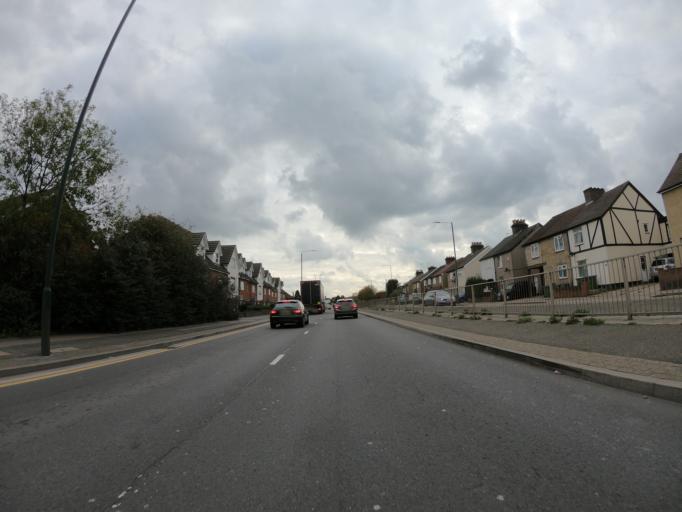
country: GB
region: England
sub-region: Greater London
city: Erith
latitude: 51.4684
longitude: 0.1811
